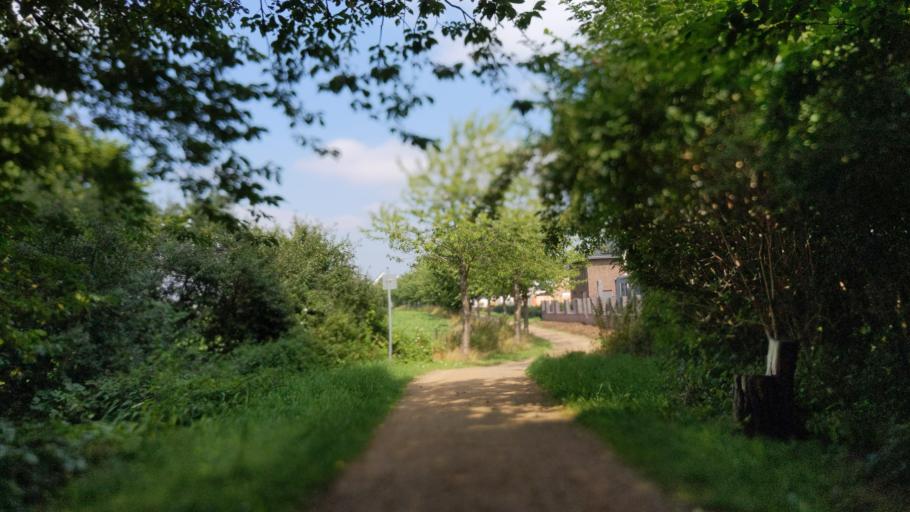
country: DE
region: Schleswig-Holstein
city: Stockelsdorf
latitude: 53.8868
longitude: 10.6340
